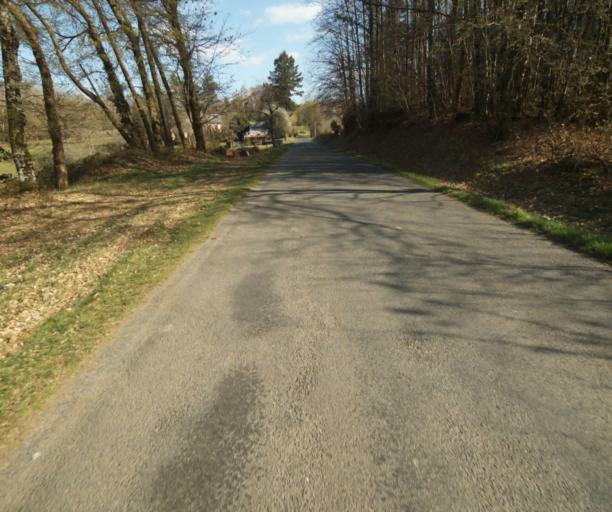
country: FR
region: Limousin
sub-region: Departement de la Correze
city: Saint-Mexant
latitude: 45.3326
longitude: 1.6217
